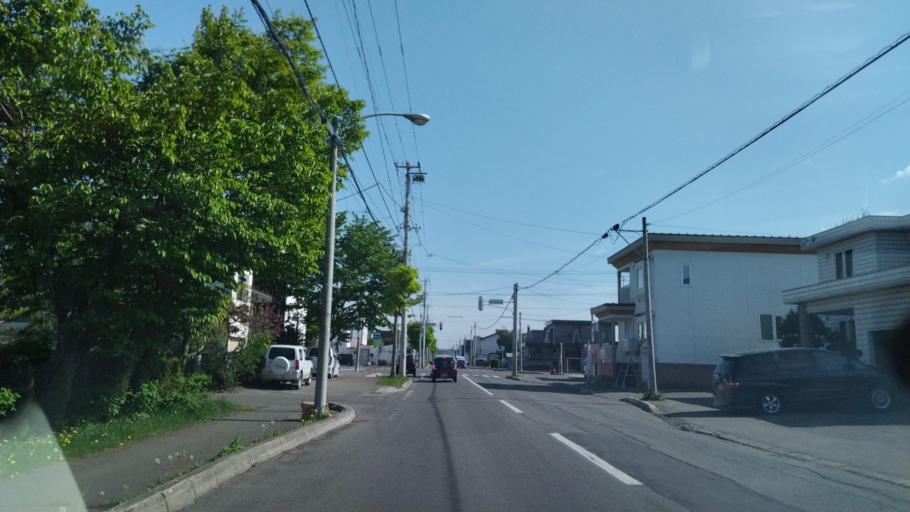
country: JP
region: Hokkaido
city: Obihiro
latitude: 42.8987
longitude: 143.1879
